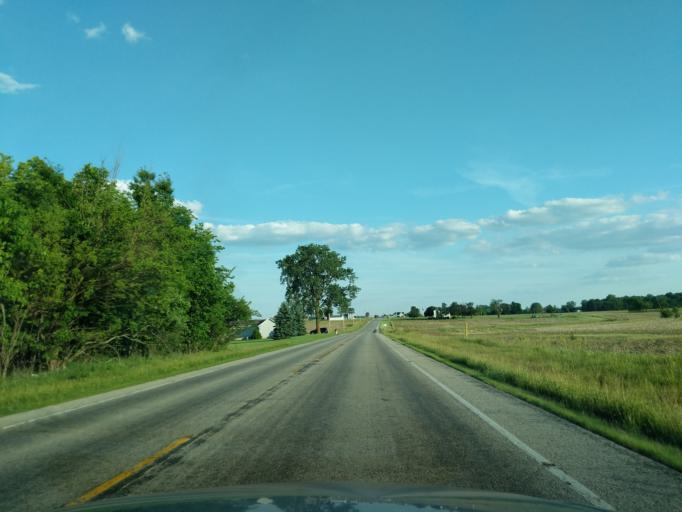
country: US
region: Indiana
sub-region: Huntington County
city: Warren
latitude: 40.7339
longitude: -85.4412
